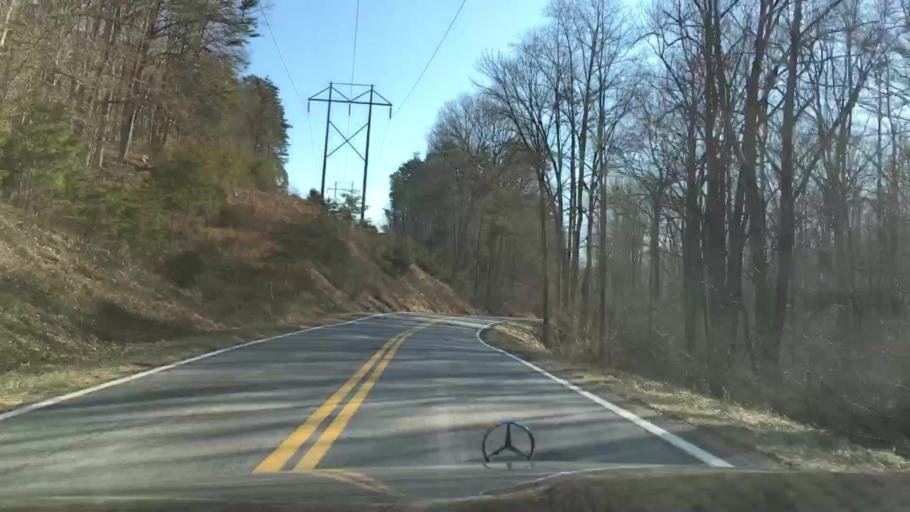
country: US
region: Virginia
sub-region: Campbell County
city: Altavista
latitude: 37.1439
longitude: -79.3304
